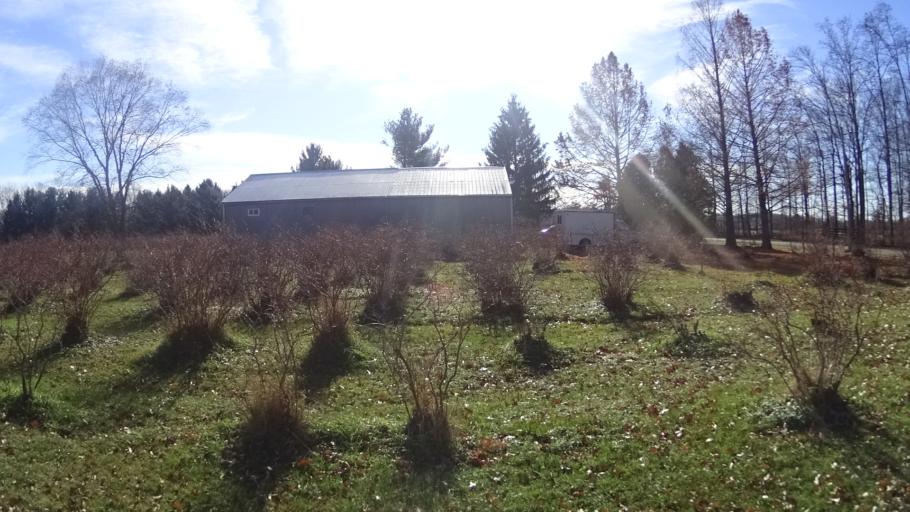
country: US
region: Ohio
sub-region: Lorain County
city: South Amherst
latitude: 41.3580
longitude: -82.3123
